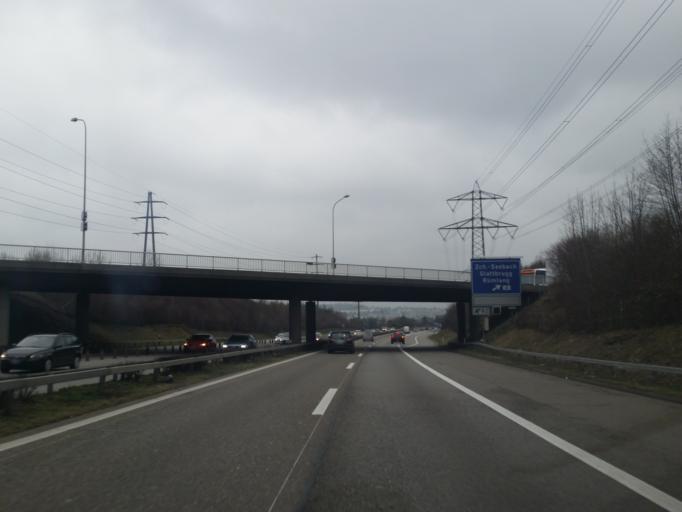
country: CH
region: Zurich
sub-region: Bezirk Zuerich
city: Zuerich (Kreis 11) / Seebach
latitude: 47.4327
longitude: 8.5424
